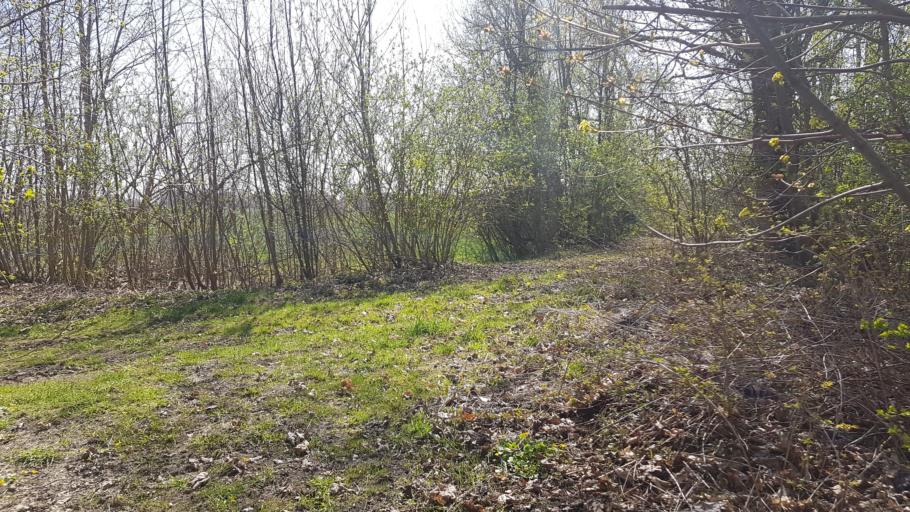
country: PL
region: Pomeranian Voivodeship
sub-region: Powiat slupski
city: Ustka
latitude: 54.5152
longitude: 16.7356
